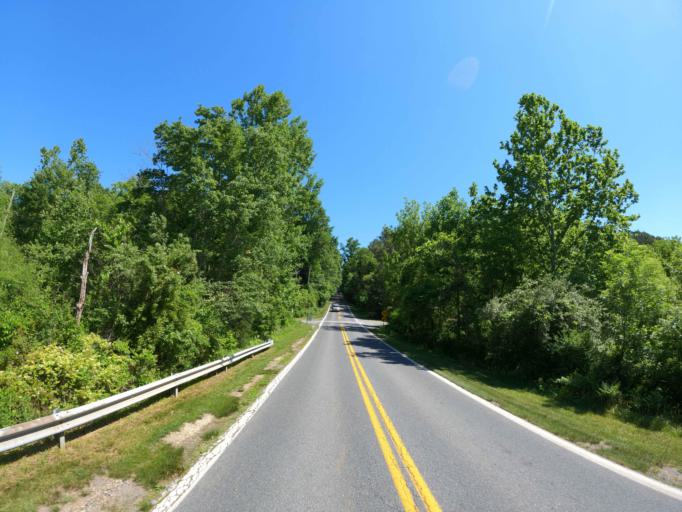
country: US
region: Maryland
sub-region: Montgomery County
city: Clarksburg
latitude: 39.2654
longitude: -77.2809
